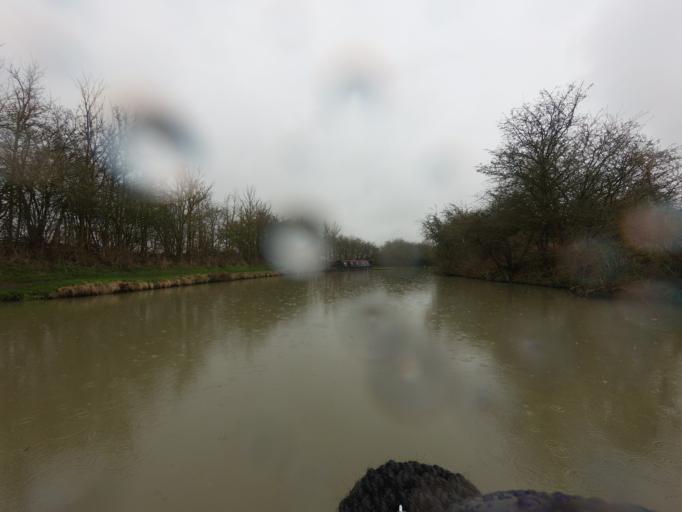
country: GB
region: England
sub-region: Northamptonshire
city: Blisworth
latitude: 52.1849
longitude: -0.9447
